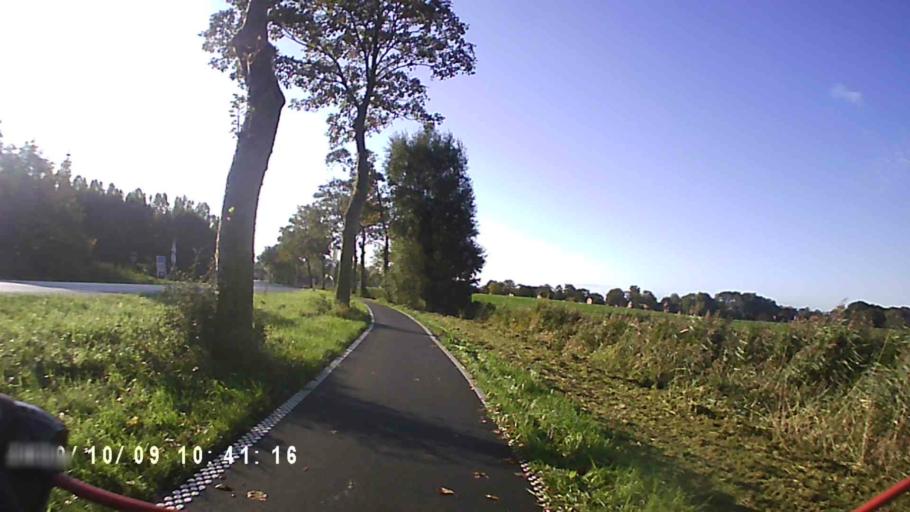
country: NL
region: Groningen
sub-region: Gemeente Winsum
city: Winsum
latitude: 53.2784
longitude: 6.5344
